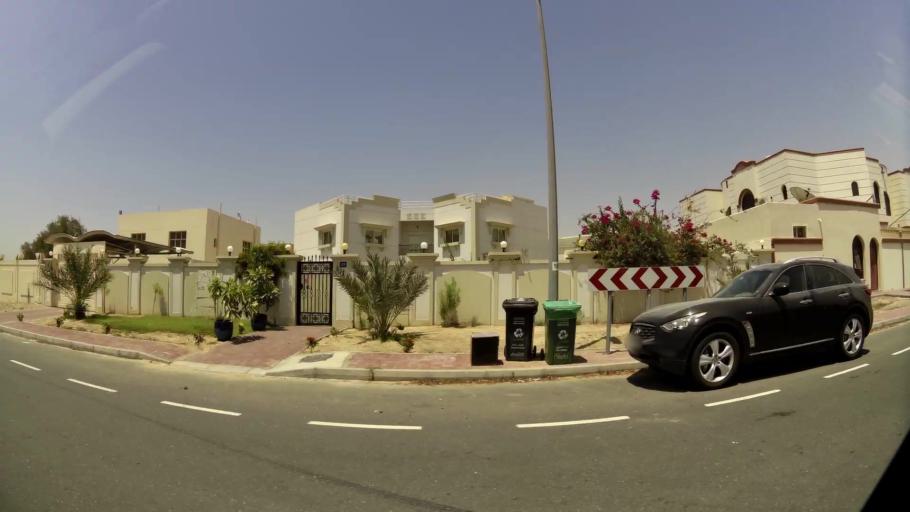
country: AE
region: Dubai
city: Dubai
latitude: 25.0915
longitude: 55.2065
